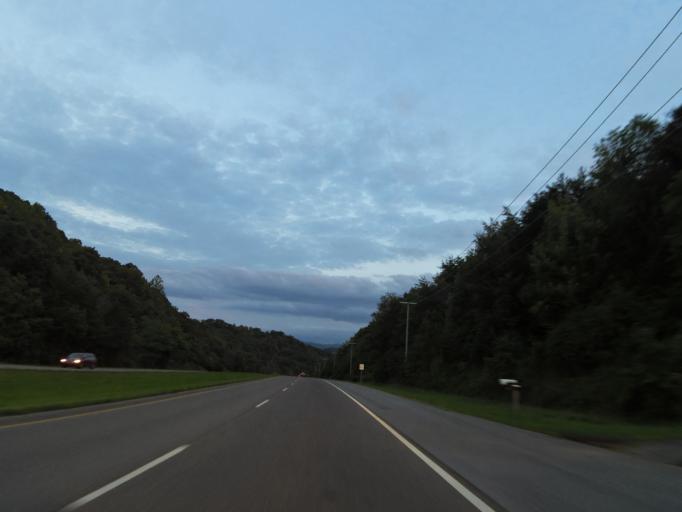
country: US
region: Tennessee
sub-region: Carter County
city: Elizabethton
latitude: 36.3706
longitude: -82.2125
